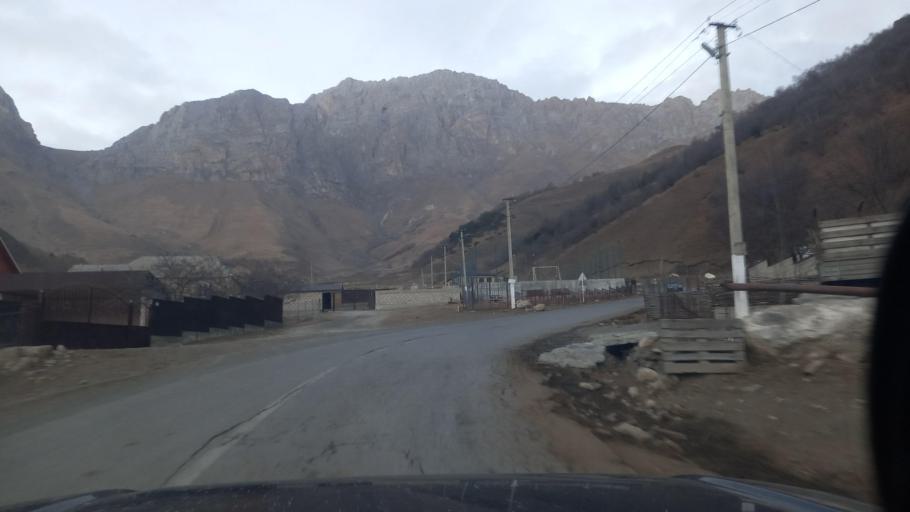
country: RU
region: Ingushetiya
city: Dzhayrakh
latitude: 42.8155
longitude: 44.8136
